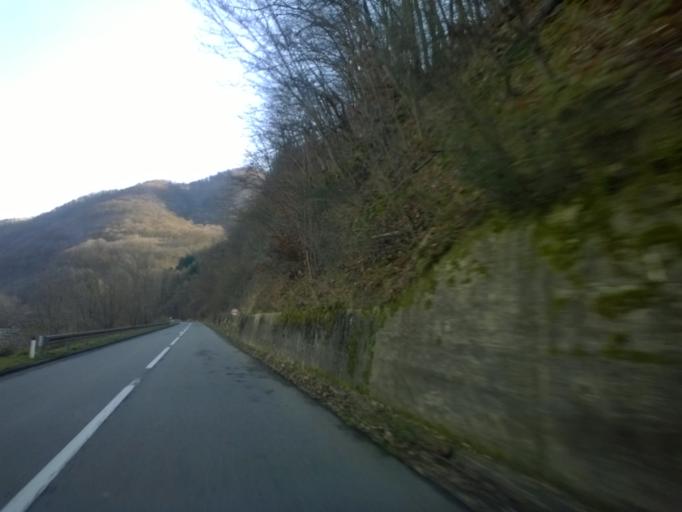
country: RS
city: Radenka
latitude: 44.6470
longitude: 21.8092
